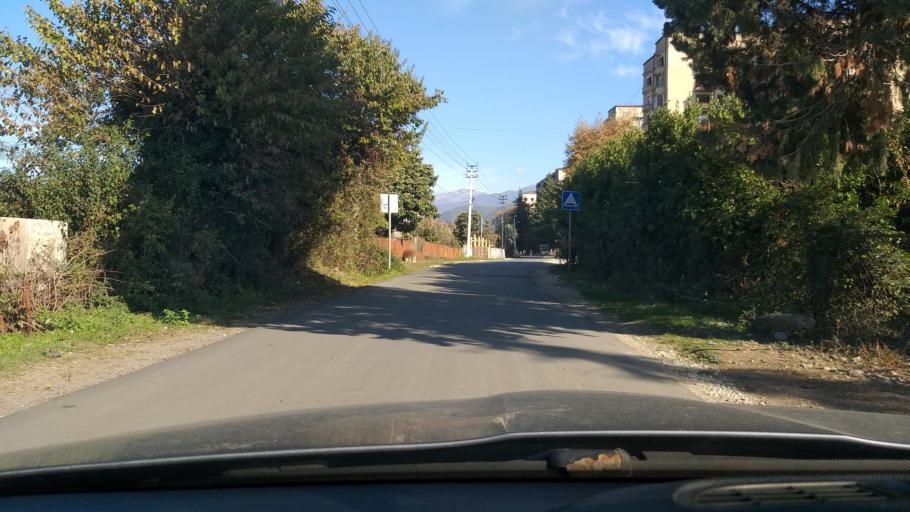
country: GE
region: Abkhazia
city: Sokhumi
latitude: 43.0159
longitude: 40.9616
